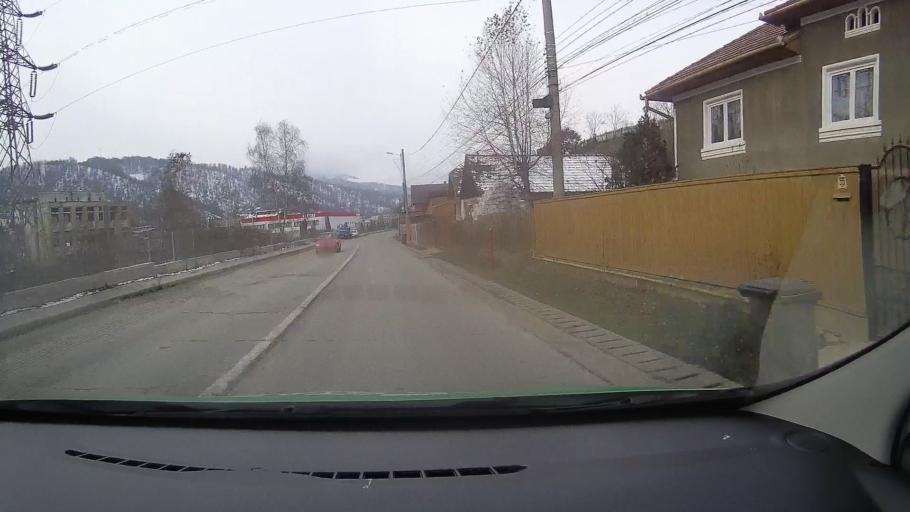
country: RO
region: Alba
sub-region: Oras Zlatna
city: Zlatna
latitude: 46.1074
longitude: 23.2346
